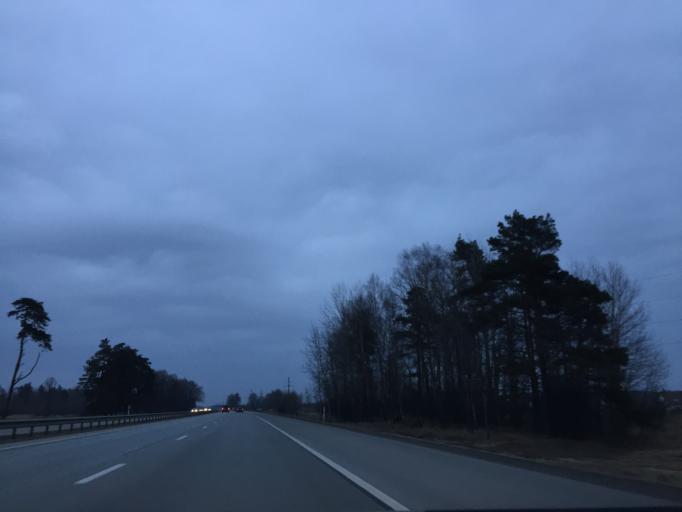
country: LV
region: Olaine
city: Olaine
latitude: 56.8170
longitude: 24.0132
